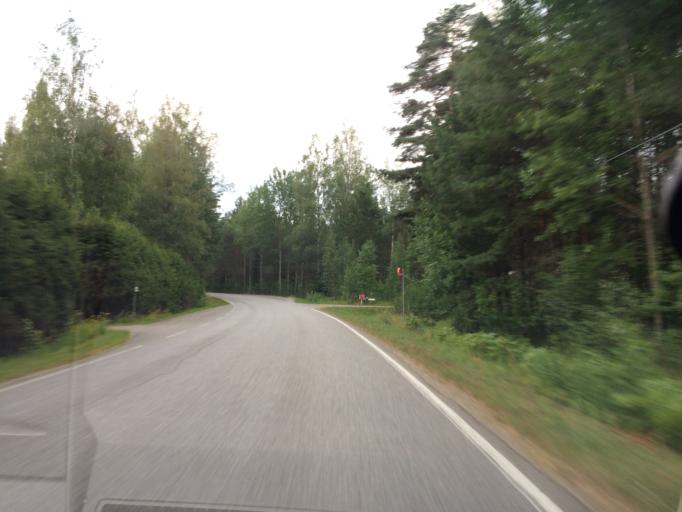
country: FI
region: Haeme
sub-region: Haemeenlinna
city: Tuulos
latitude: 61.2139
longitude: 24.7303
